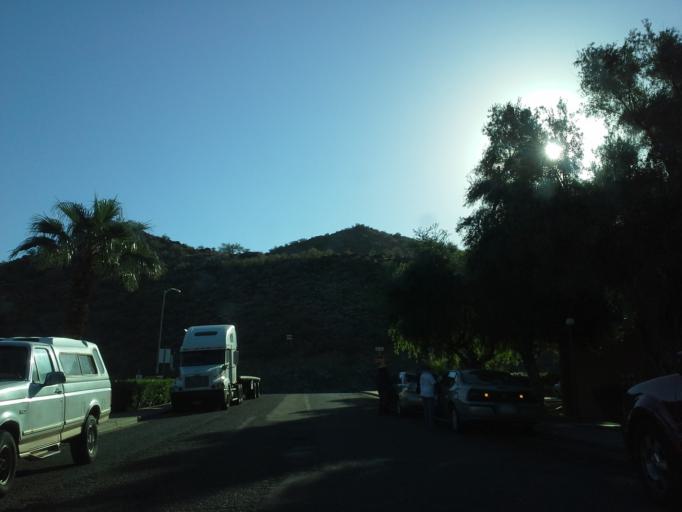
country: US
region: Arizona
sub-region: Maricopa County
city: Glendale
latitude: 33.6002
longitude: -112.1013
